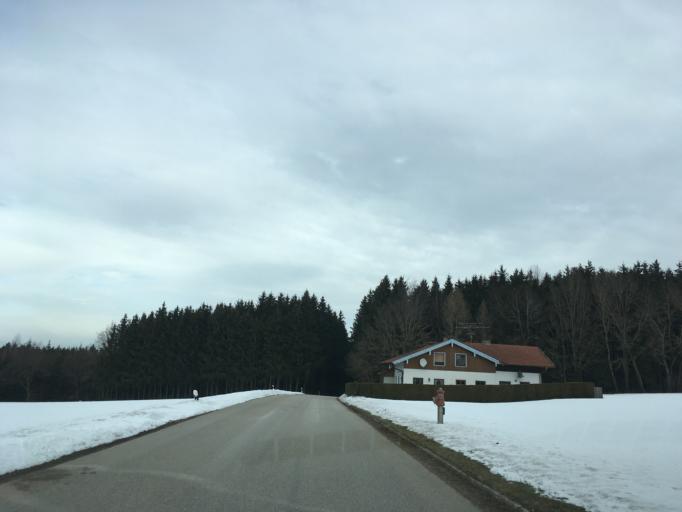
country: DE
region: Bavaria
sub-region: Upper Bavaria
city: Unterreit
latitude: 48.1161
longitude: 12.3796
